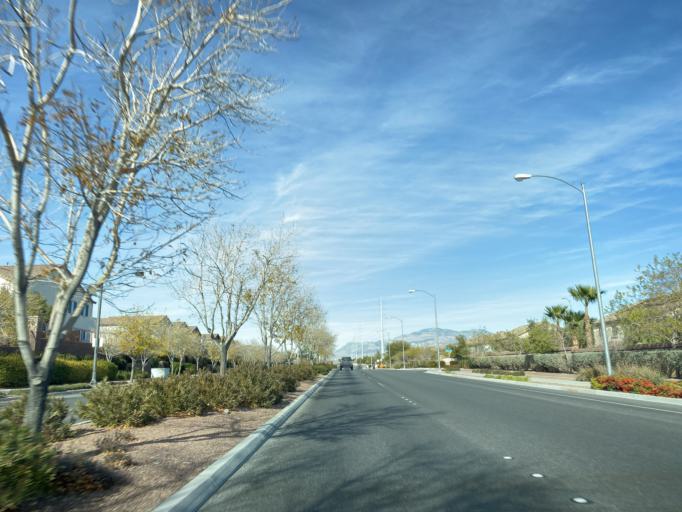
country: US
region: Nevada
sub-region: Clark County
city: Summerlin South
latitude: 36.2968
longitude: -115.3149
